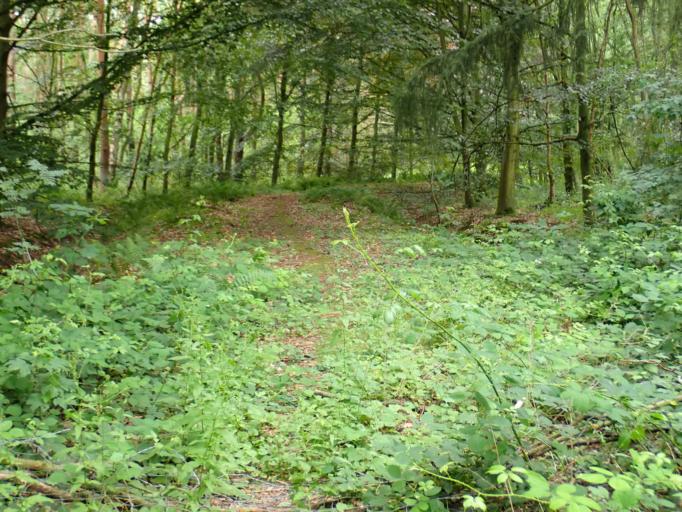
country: BE
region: Flanders
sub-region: Provincie Vlaams-Brabant
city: Haacht
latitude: 50.9689
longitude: 4.6481
